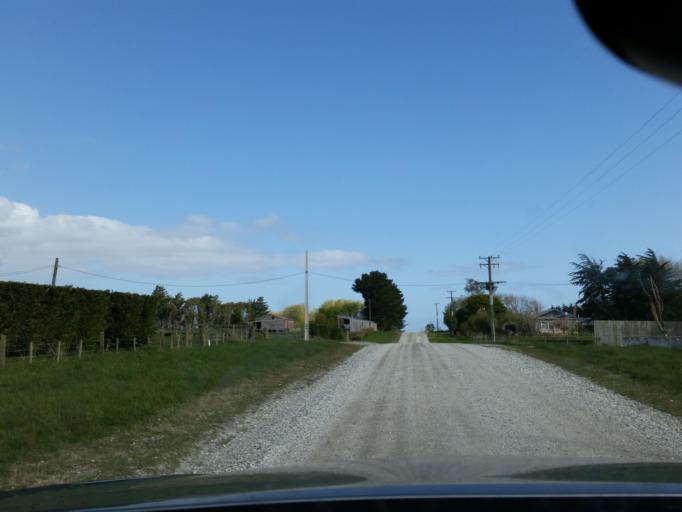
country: NZ
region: Southland
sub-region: Invercargill City
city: Invercargill
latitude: -46.4156
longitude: 168.5061
